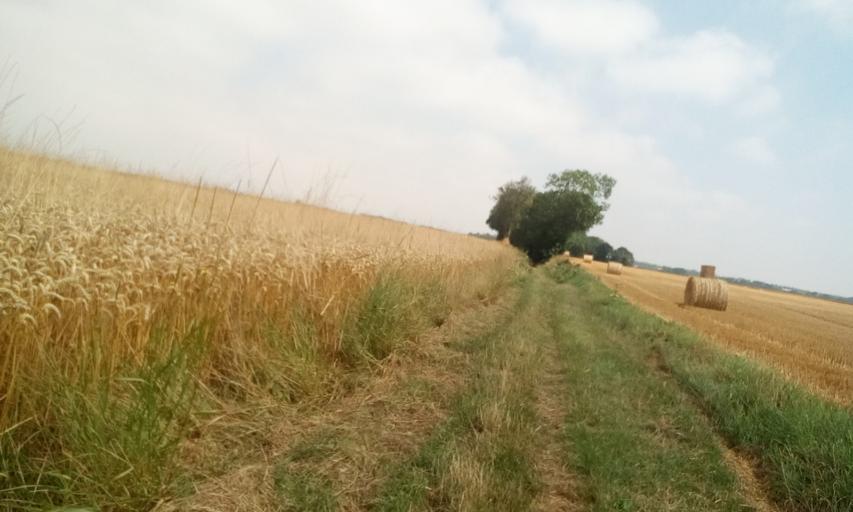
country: FR
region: Lower Normandy
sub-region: Departement du Calvados
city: Douvres-la-Delivrande
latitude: 49.2966
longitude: -0.4068
